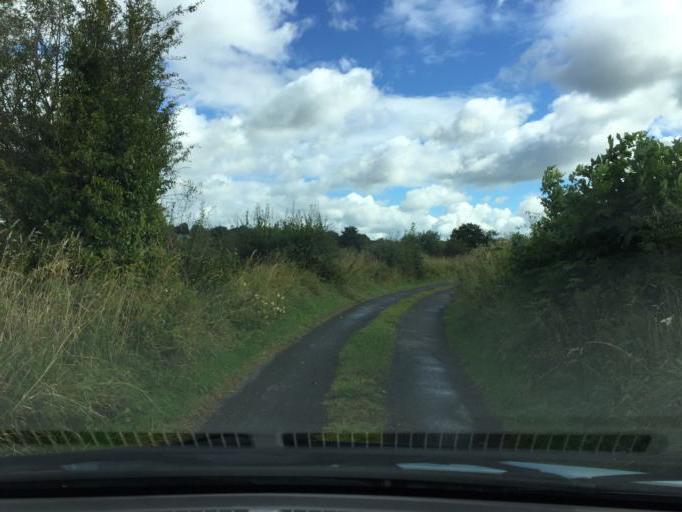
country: IE
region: Connaught
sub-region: Maigh Eo
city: Swinford
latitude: 54.0325
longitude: -8.9005
